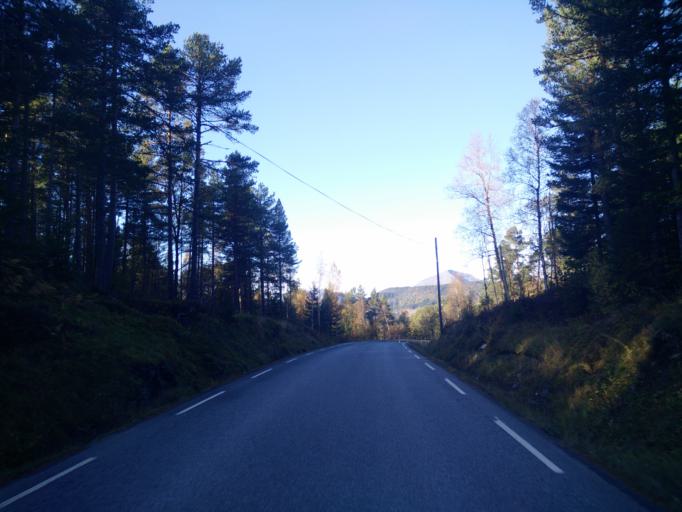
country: NO
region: More og Romsdal
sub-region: Halsa
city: Liaboen
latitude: 63.1021
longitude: 8.3367
